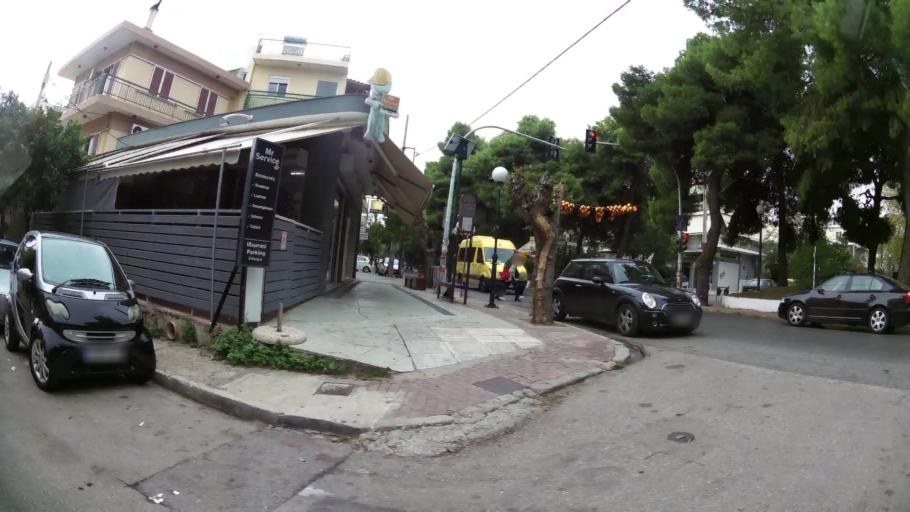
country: GR
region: Attica
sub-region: Nomarchia Athinas
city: Chaidari
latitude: 38.0089
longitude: 23.6653
